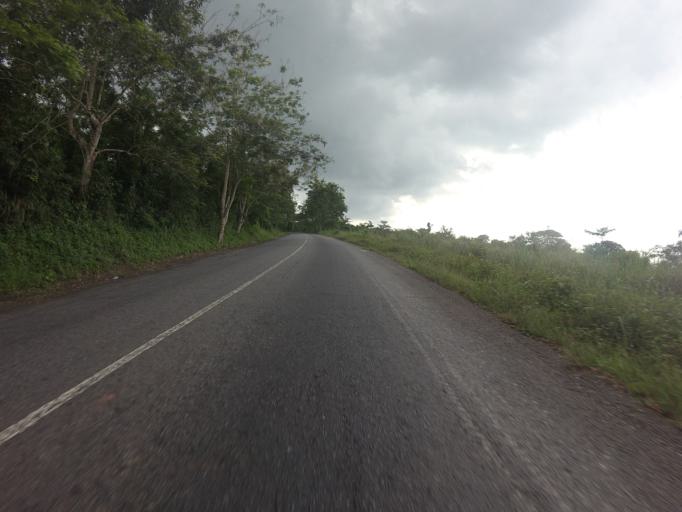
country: GH
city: Akropong
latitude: 5.9548
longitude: -0.1172
